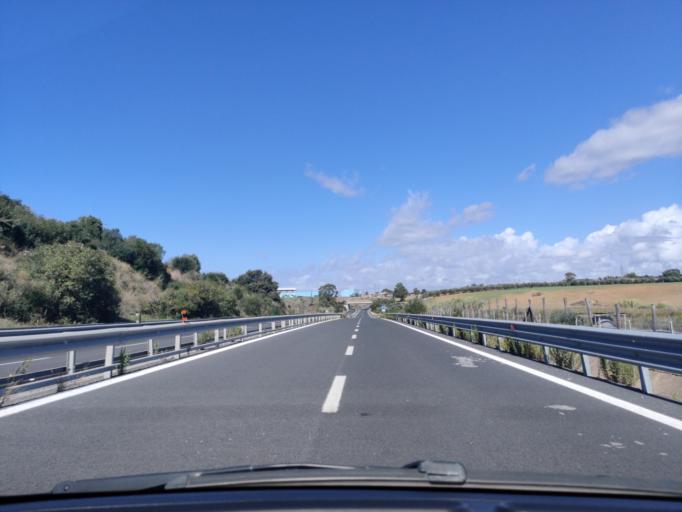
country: IT
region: Latium
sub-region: Citta metropolitana di Roma Capitale
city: Civitavecchia
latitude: 42.1158
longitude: 11.7921
